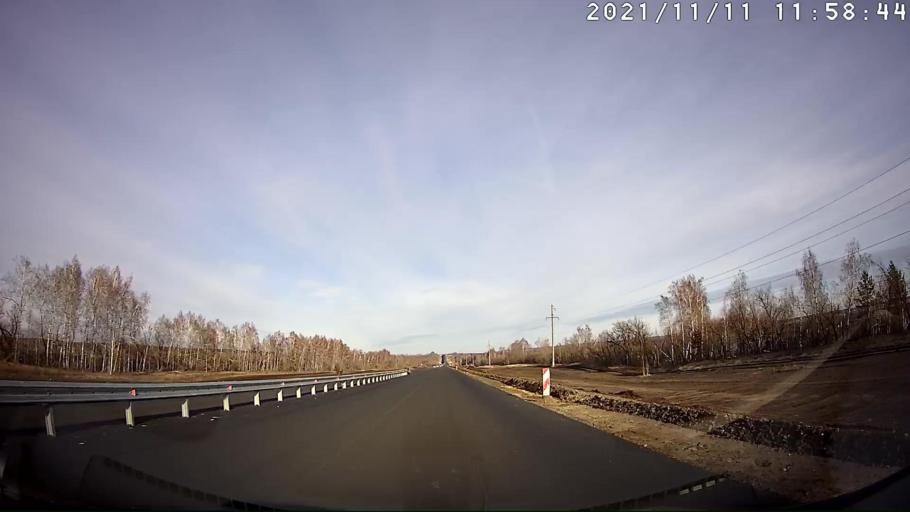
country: RU
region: Samara
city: Balasheyka
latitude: 53.5843
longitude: 48.3332
